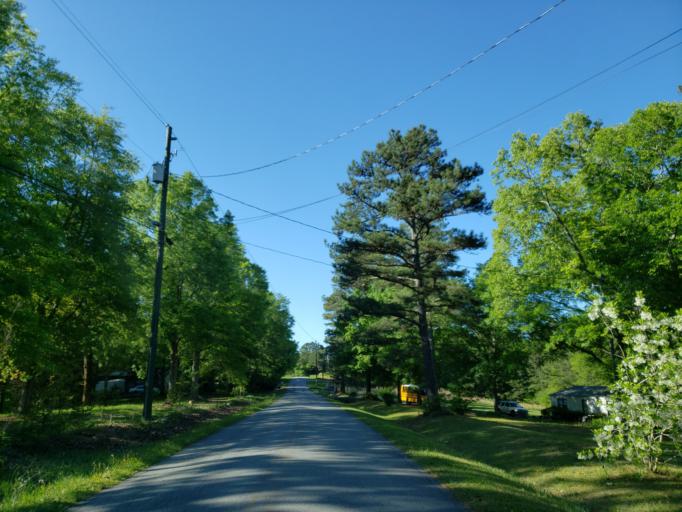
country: US
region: Georgia
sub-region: Polk County
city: Aragon
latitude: 34.0131
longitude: -85.1452
